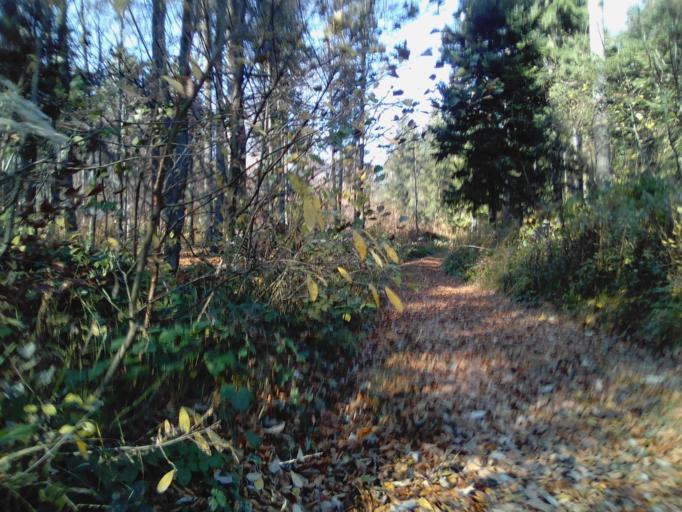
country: PL
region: Subcarpathian Voivodeship
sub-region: Powiat krosnienski
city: Leki
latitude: 49.8294
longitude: 21.6846
